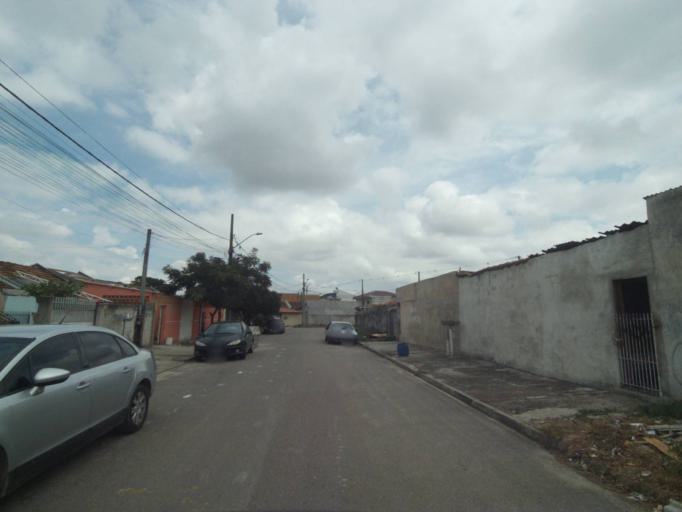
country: BR
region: Parana
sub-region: Pinhais
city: Pinhais
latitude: -25.4637
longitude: -49.1927
